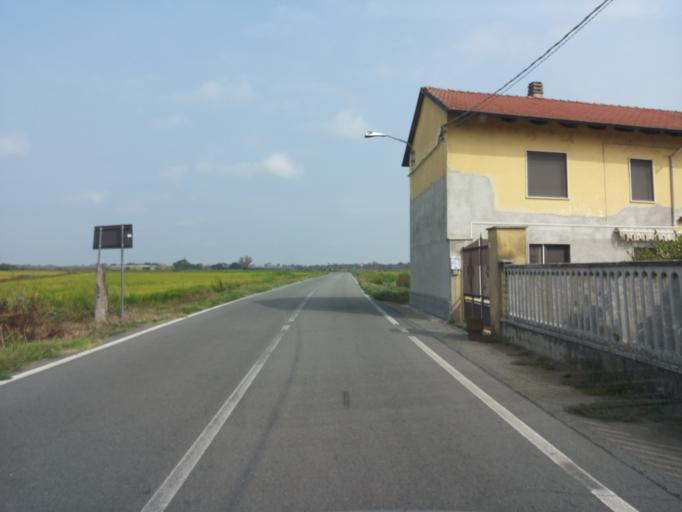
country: IT
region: Piedmont
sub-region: Provincia di Vercelli
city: Prarolo
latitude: 45.2851
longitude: 8.4770
